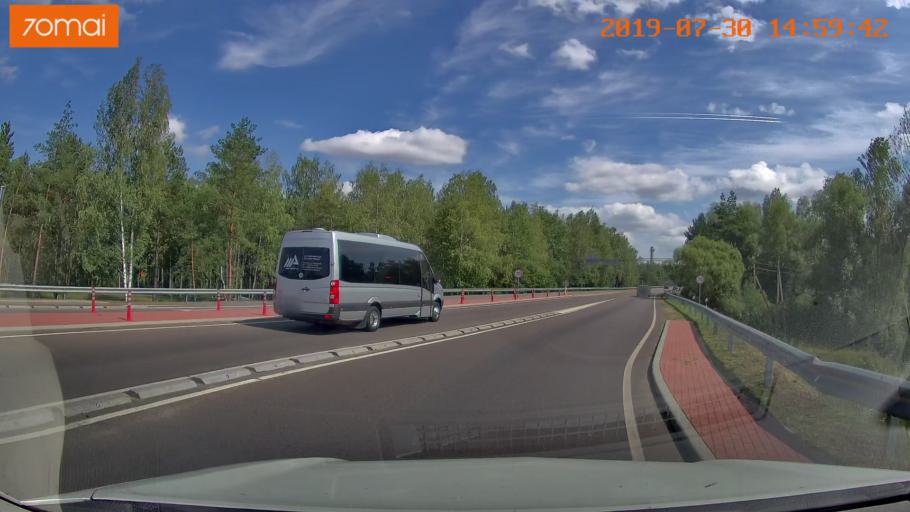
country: LT
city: Birstonas
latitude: 54.6066
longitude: 24.0131
